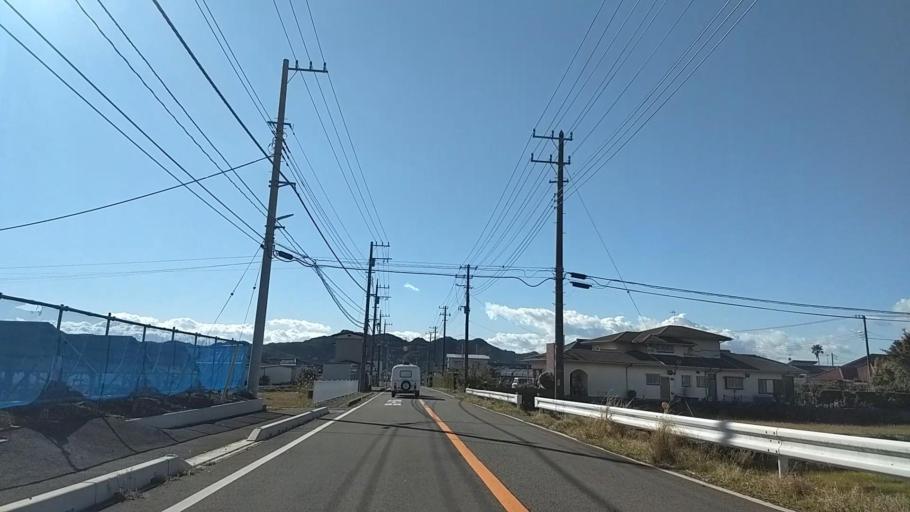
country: JP
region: Chiba
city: Tateyama
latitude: 34.9358
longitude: 139.8405
